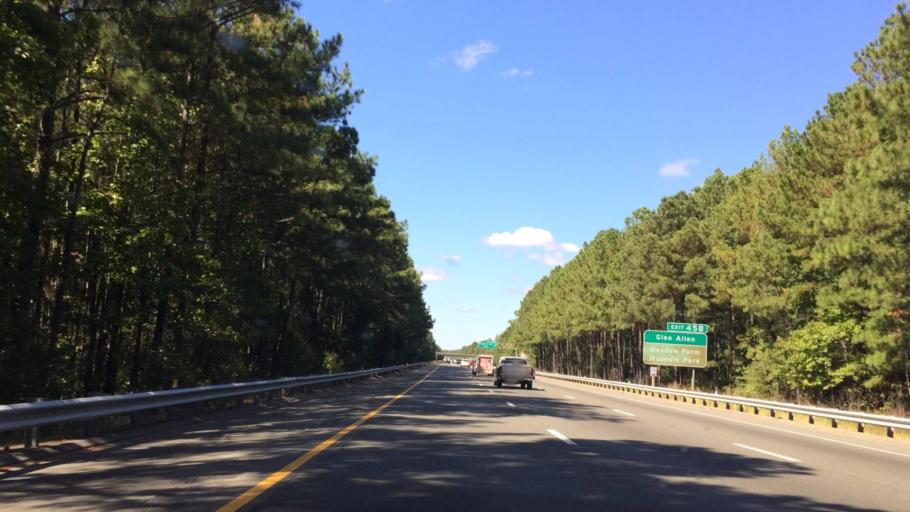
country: US
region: Virginia
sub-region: Henrico County
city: Glen Allen
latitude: 37.6632
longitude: -77.4772
